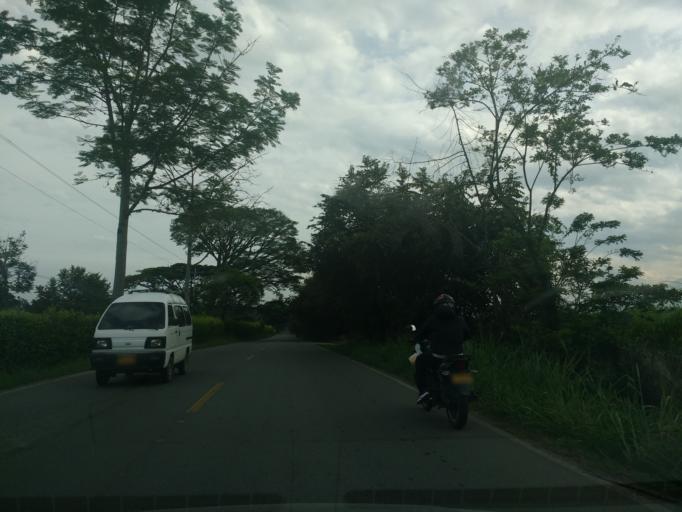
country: CO
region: Valle del Cauca
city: Florida
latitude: 3.3029
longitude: -76.2324
